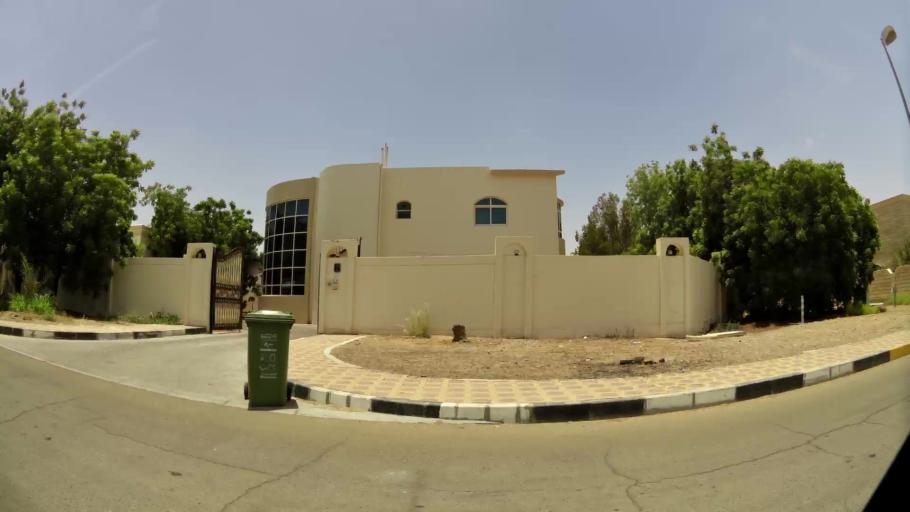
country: OM
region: Al Buraimi
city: Al Buraymi
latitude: 24.2801
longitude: 55.7349
